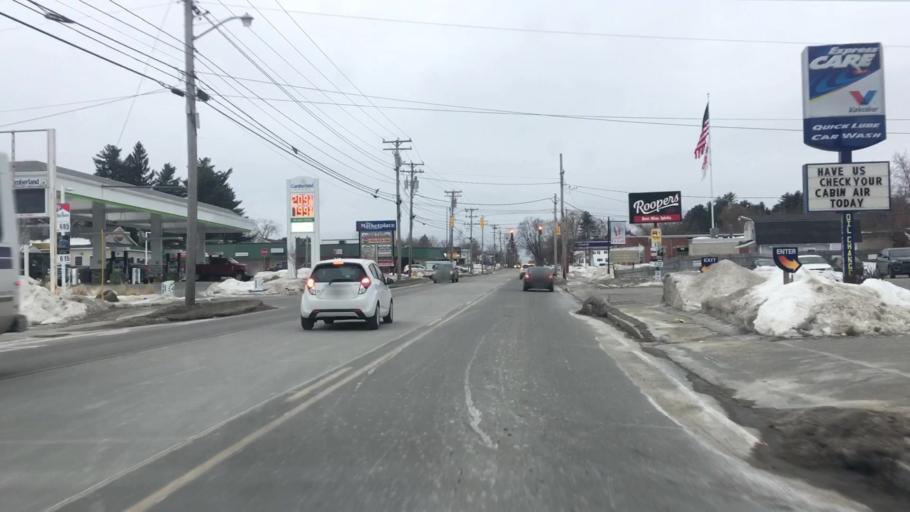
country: US
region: Maine
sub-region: Androscoggin County
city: Lewiston
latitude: 44.1218
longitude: -70.2024
